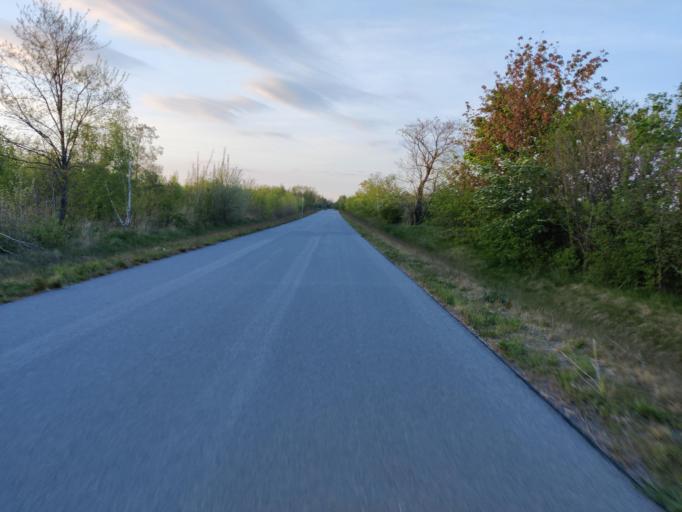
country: DE
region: Saxony
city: Zwenkau
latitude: 51.2173
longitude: 12.3590
